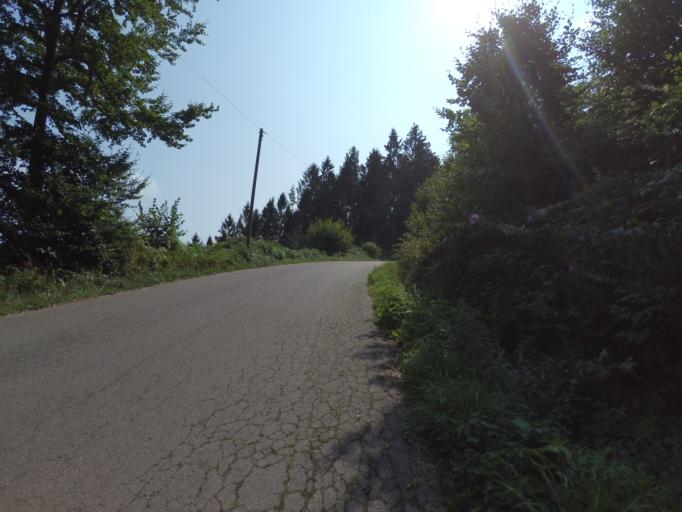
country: DE
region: Rheinland-Pfalz
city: Taben-Rodt
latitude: 49.5414
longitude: 6.5907
